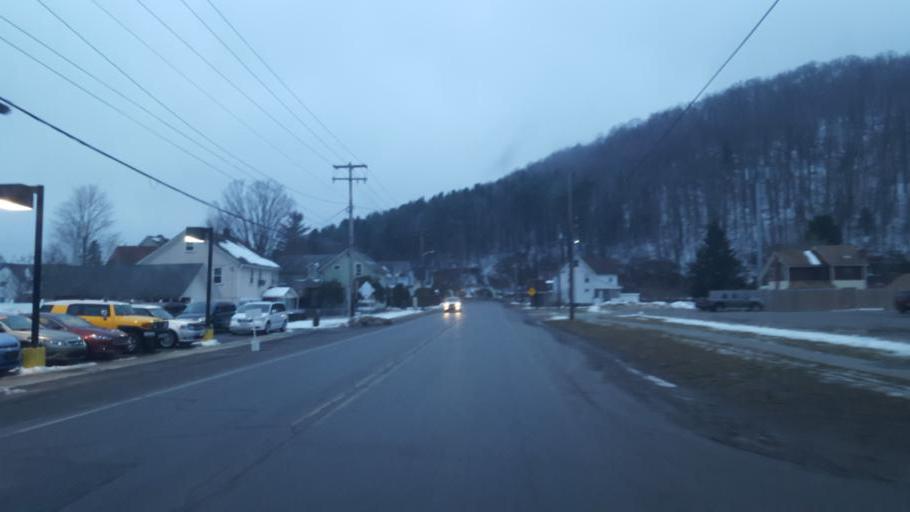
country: US
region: Pennsylvania
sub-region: Potter County
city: Coudersport
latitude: 41.7697
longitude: -78.0225
